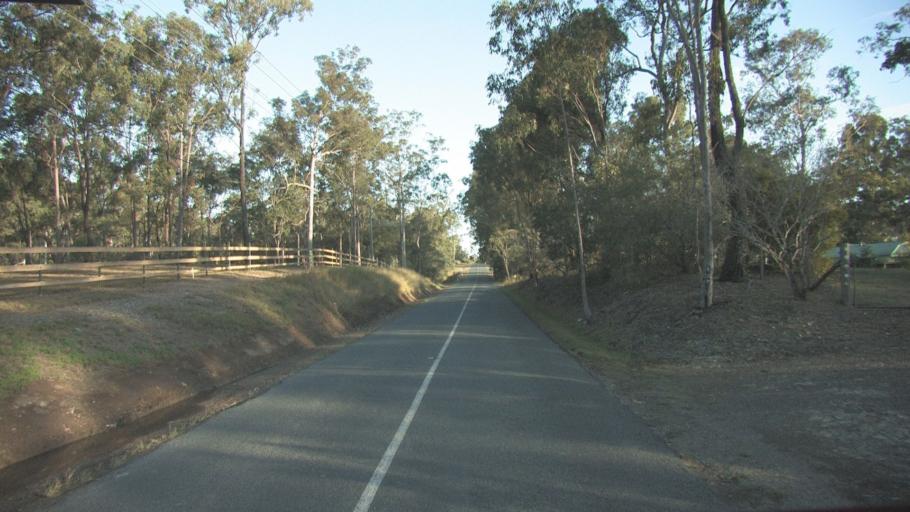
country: AU
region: Queensland
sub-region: Logan
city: Waterford West
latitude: -27.7291
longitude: 153.1466
